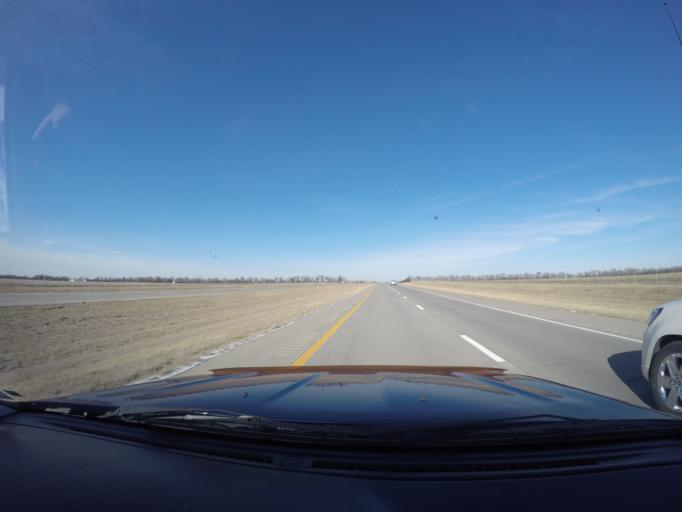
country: US
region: Kansas
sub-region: Sedgwick County
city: Valley Center
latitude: 37.8865
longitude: -97.3265
